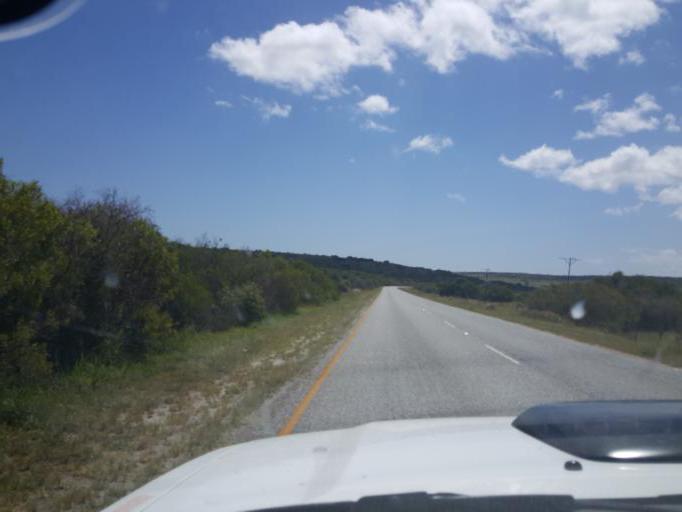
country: ZA
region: Eastern Cape
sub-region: Cacadu District Municipality
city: Grahamstown
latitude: -33.5345
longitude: 26.0687
